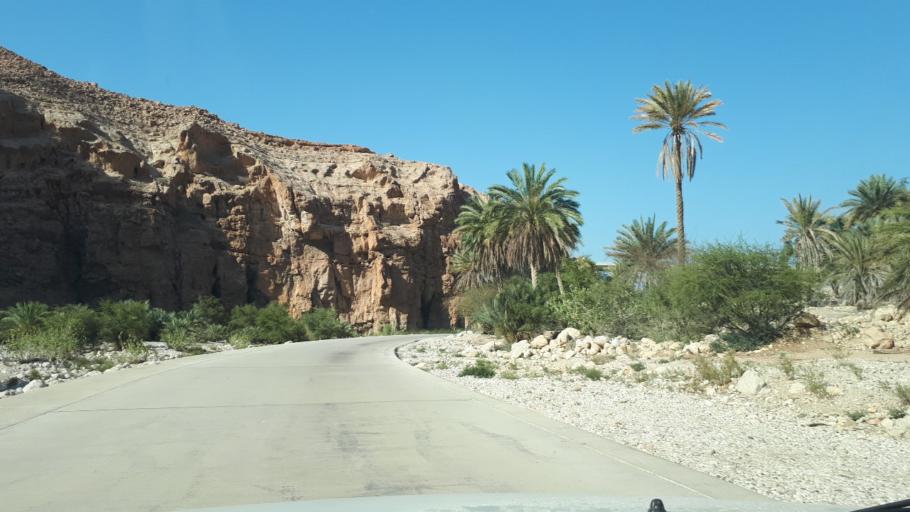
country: OM
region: Ash Sharqiyah
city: Sur
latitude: 22.8219
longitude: 59.2580
